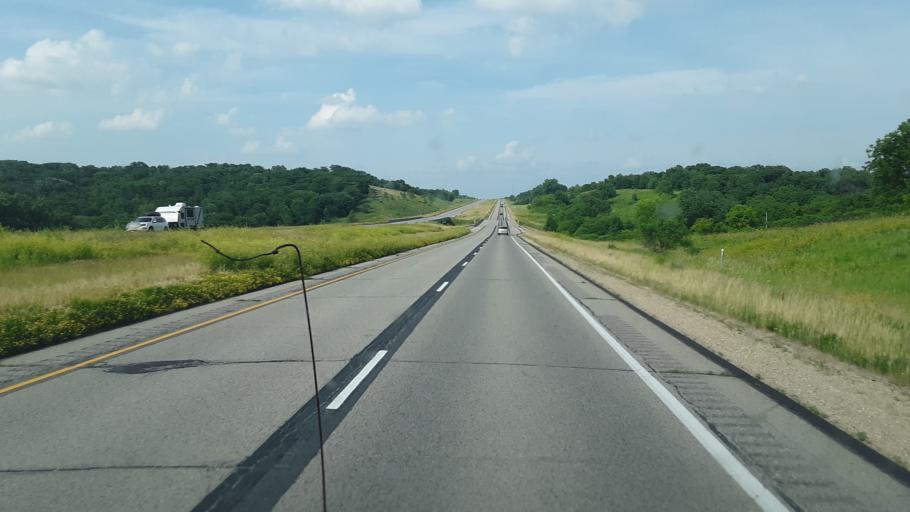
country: US
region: Iowa
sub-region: Jasper County
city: Baxter
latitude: 41.8531
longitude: -93.2475
